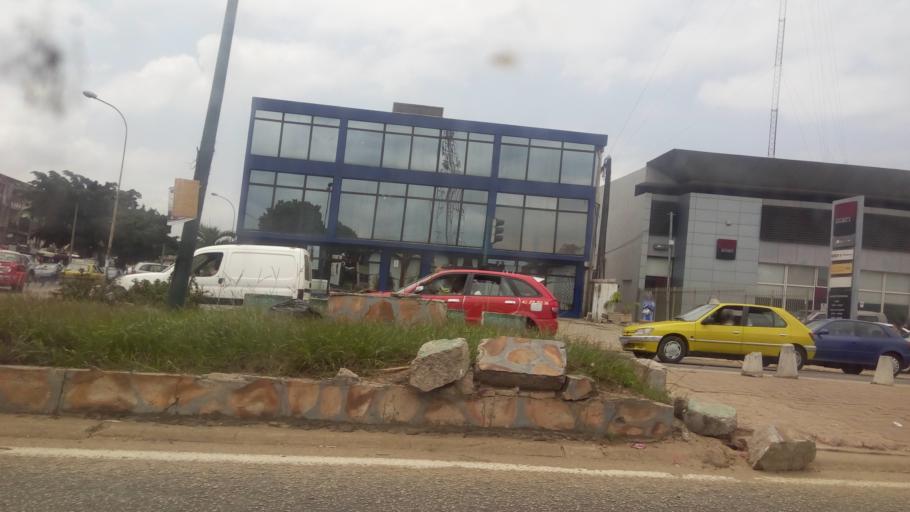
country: CI
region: Lagunes
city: Abidjan
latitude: 5.3398
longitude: -4.0036
